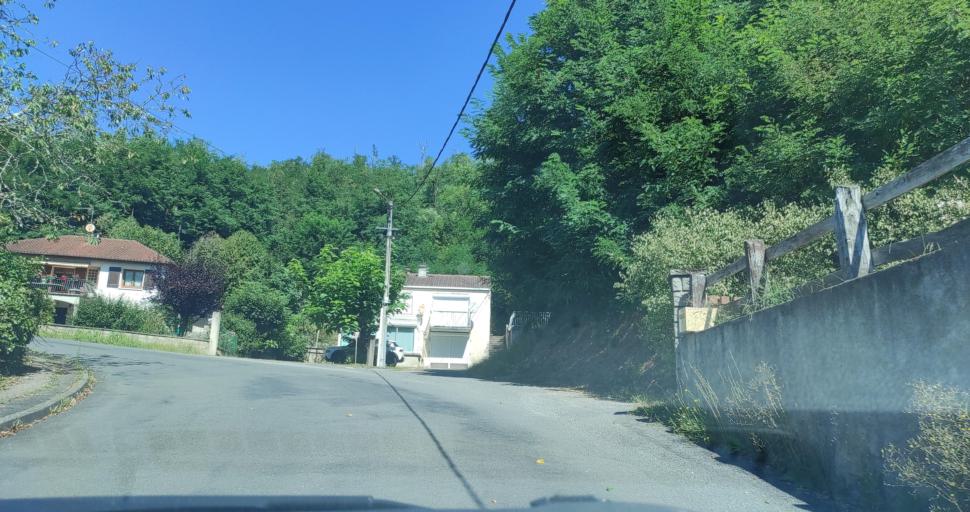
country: FR
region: Midi-Pyrenees
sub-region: Departement de l'Aveyron
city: Cransac
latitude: 44.5278
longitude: 2.2798
